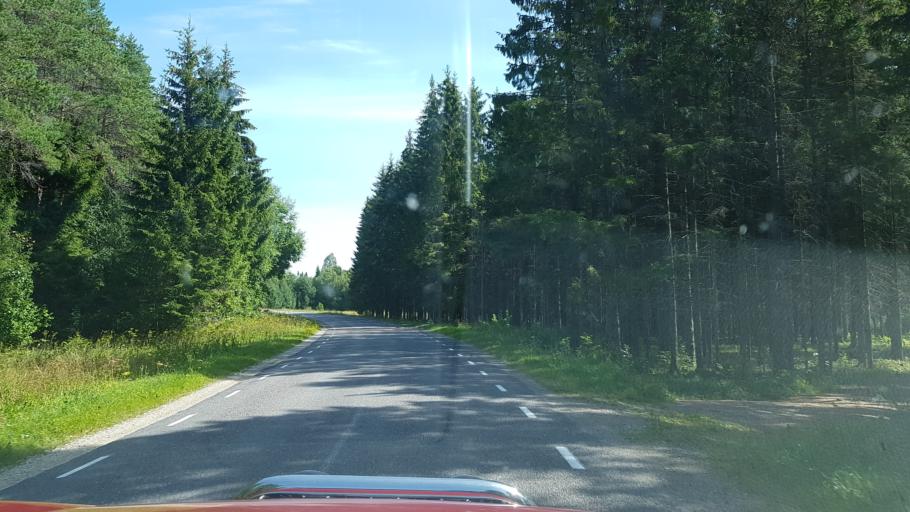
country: EE
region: Laeaene-Virumaa
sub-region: Tapa vald
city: Tapa
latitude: 59.1768
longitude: 25.9887
